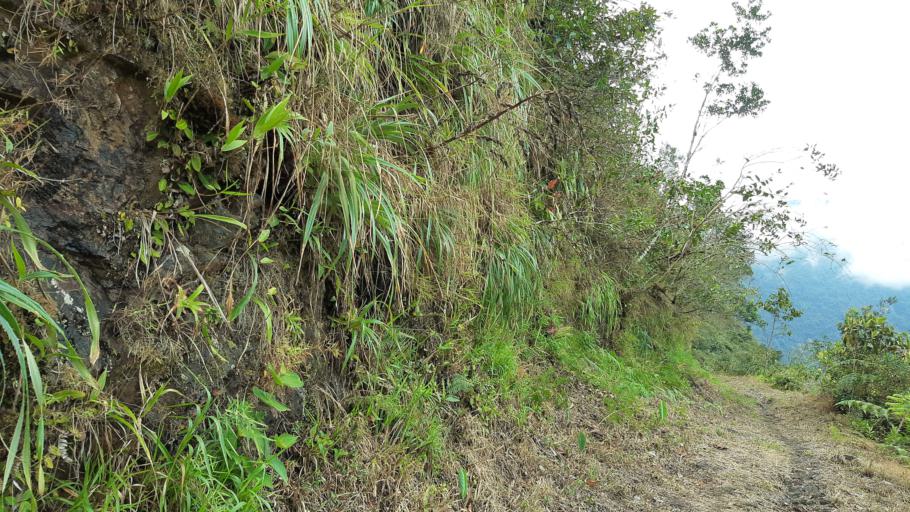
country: CO
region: Boyaca
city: Santa Maria
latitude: 4.9142
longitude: -73.3023
